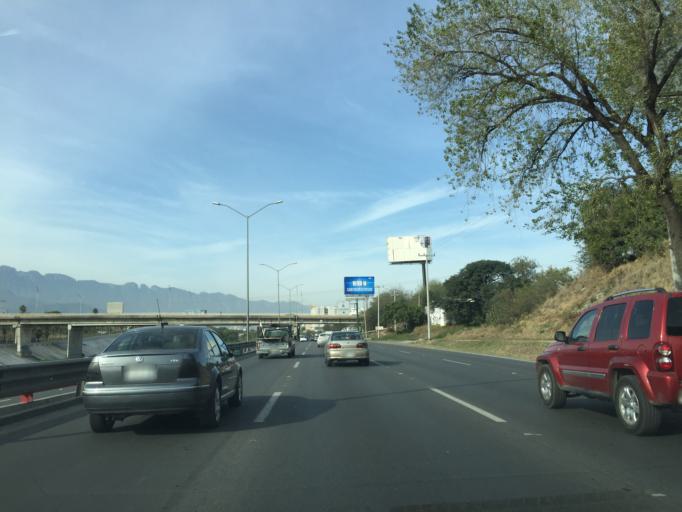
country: MX
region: Nuevo Leon
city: Guadalupe
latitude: 25.6938
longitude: -100.2275
